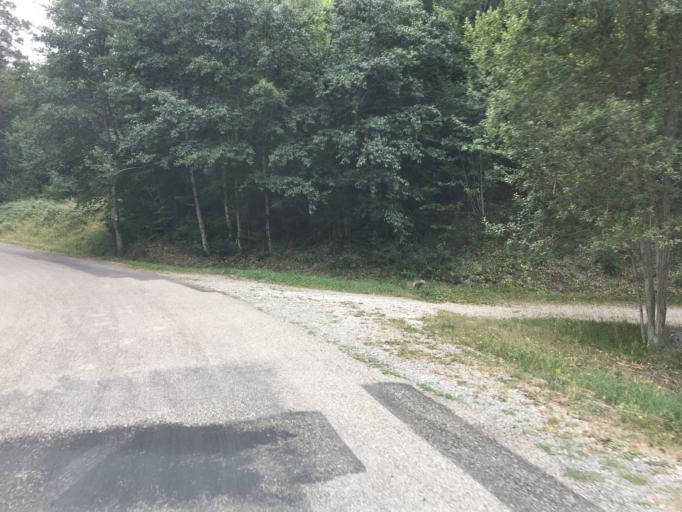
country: FR
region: Provence-Alpes-Cote d'Azur
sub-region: Departement des Alpes-de-Haute-Provence
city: Digne-les-Bains
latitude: 44.2192
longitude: 6.1399
